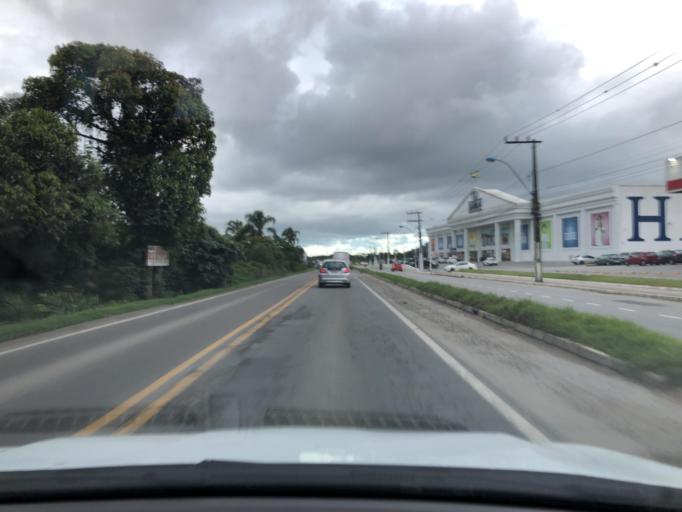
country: BR
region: Santa Catarina
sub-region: Sao Francisco Do Sul
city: Sao Francisco do Sul
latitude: -26.2543
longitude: -48.6200
